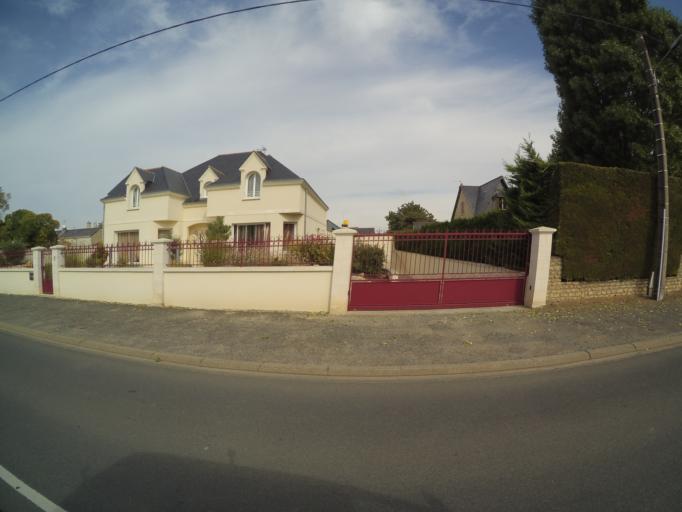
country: FR
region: Pays de la Loire
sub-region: Departement de Maine-et-Loire
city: Doue-la-Fontaine
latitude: 47.1943
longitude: -0.2961
